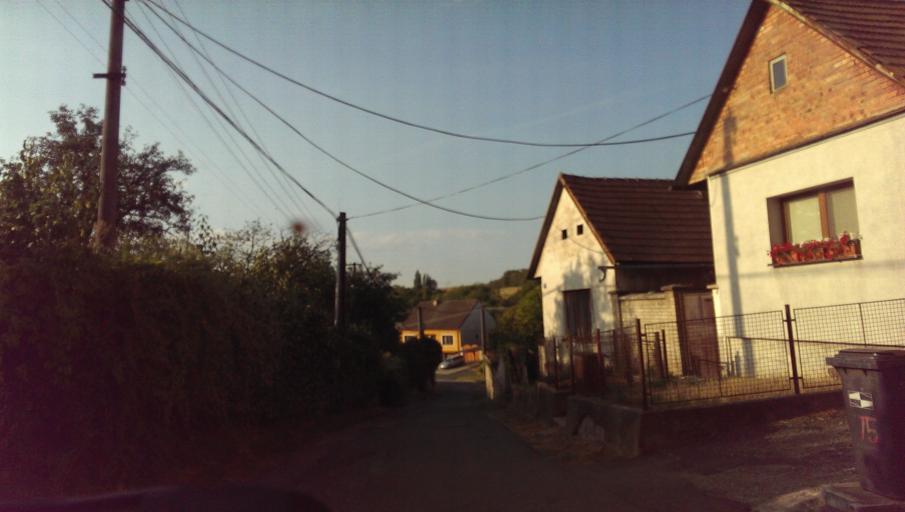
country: CZ
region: South Moravian
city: Zeravice
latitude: 49.0500
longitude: 17.2711
